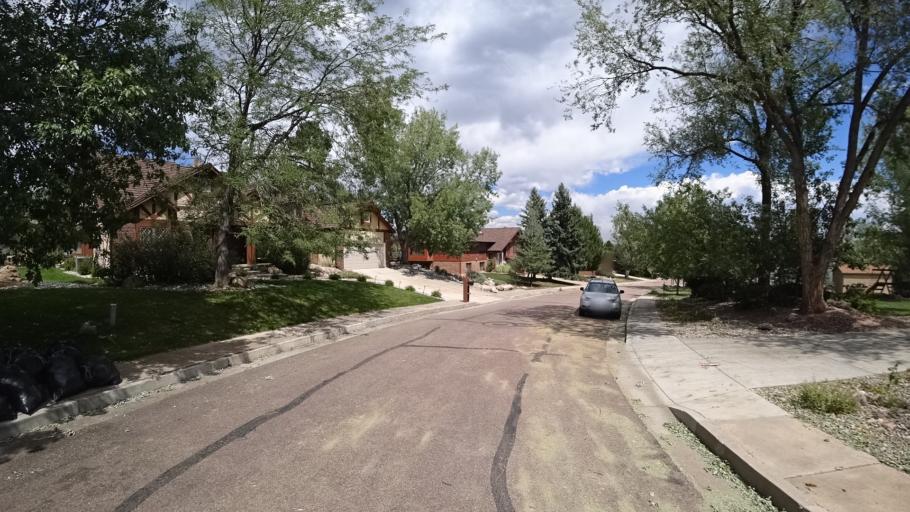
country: US
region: Colorado
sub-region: El Paso County
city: Stratmoor
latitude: 38.7688
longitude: -104.8183
